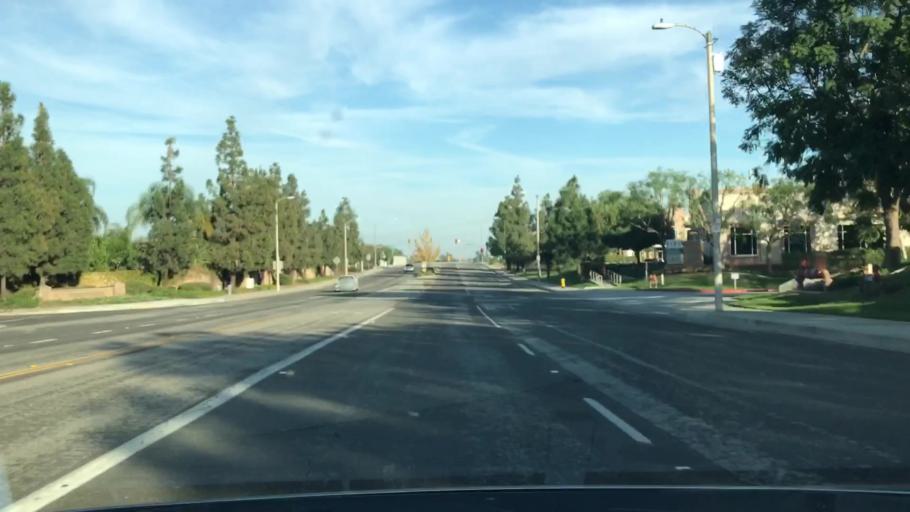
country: US
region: California
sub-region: San Bernardino County
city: Los Serranos
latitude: 33.9474
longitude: -117.6778
